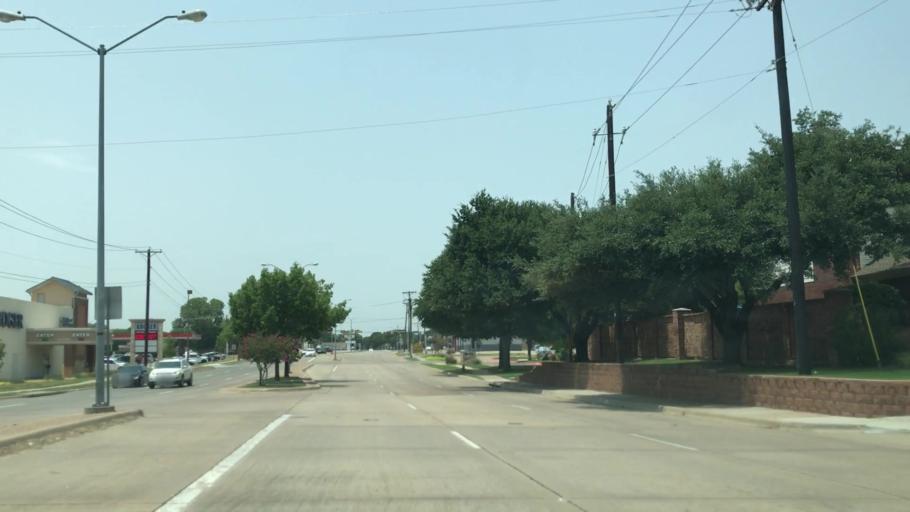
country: US
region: Texas
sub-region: Tarrant County
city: Euless
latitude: 32.8517
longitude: -97.0798
